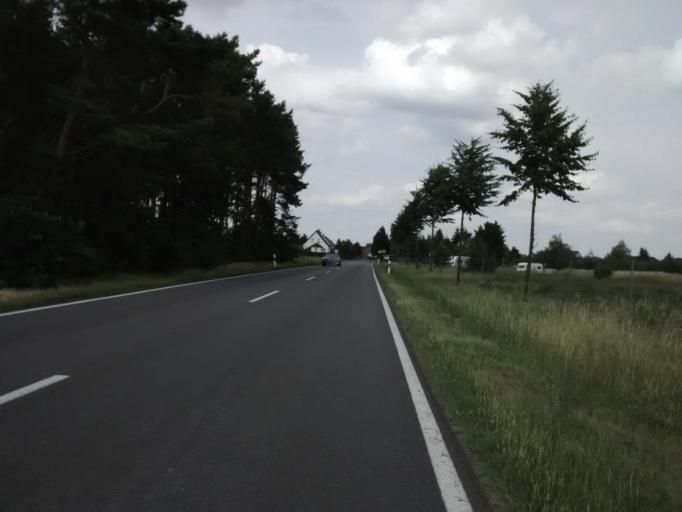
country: DE
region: Saxony-Anhalt
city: Hohenwarthe
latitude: 52.2572
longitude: 11.7554
